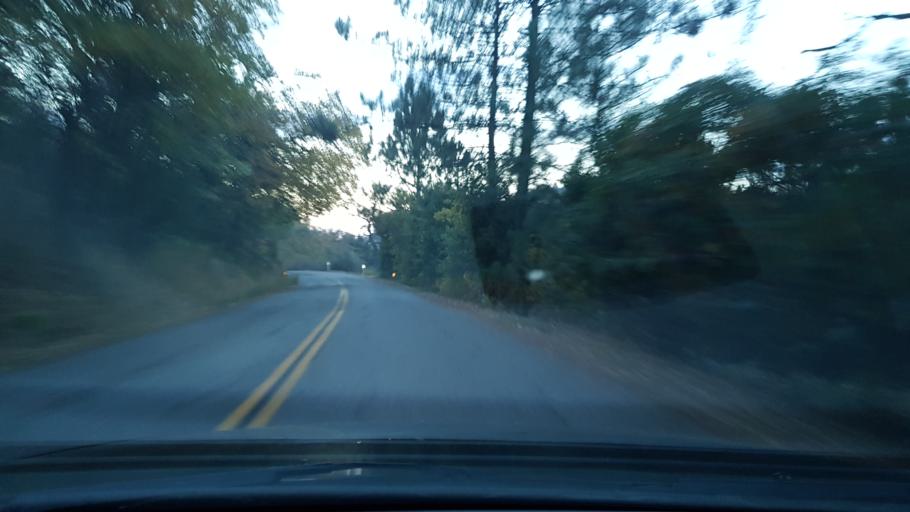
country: US
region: California
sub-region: San Diego County
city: Julian
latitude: 33.0965
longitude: -116.6145
